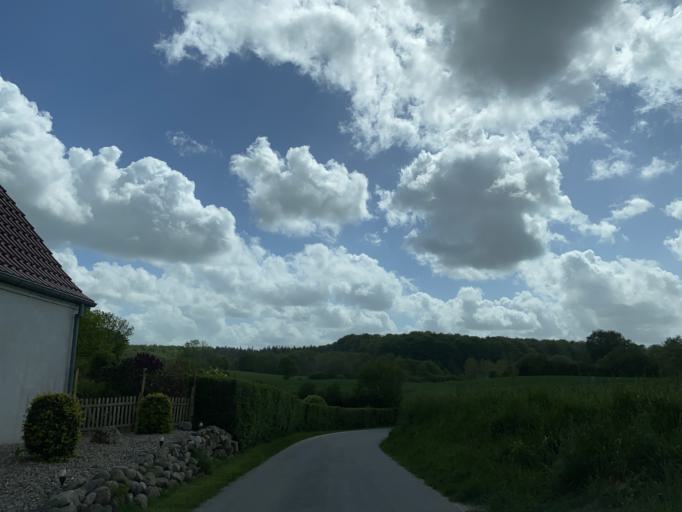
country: DK
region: South Denmark
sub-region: Aabenraa Kommune
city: Aabenraa
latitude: 55.0076
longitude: 9.4798
